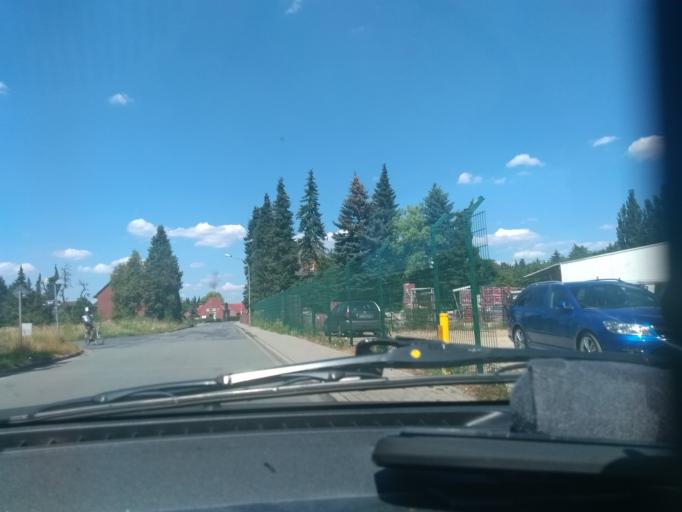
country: DE
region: Lower Saxony
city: Meppen
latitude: 52.6991
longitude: 7.2910
